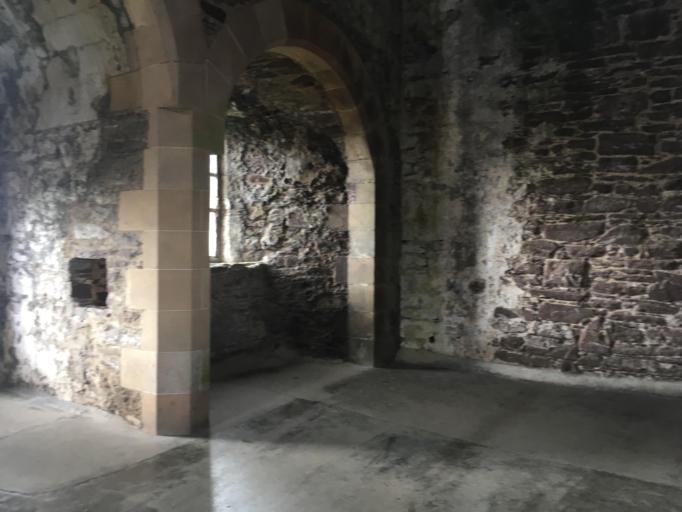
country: GB
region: Scotland
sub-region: Stirling
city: Doune
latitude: 56.1853
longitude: -4.0499
